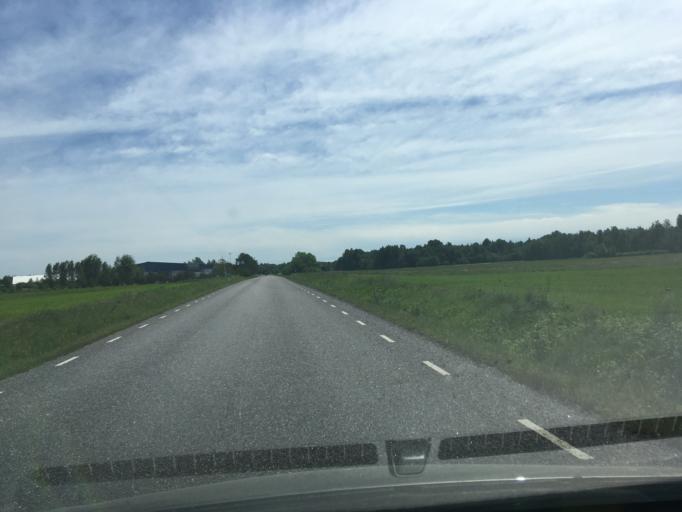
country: EE
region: Paernumaa
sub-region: Audru vald
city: Audru
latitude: 58.4274
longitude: 24.4217
